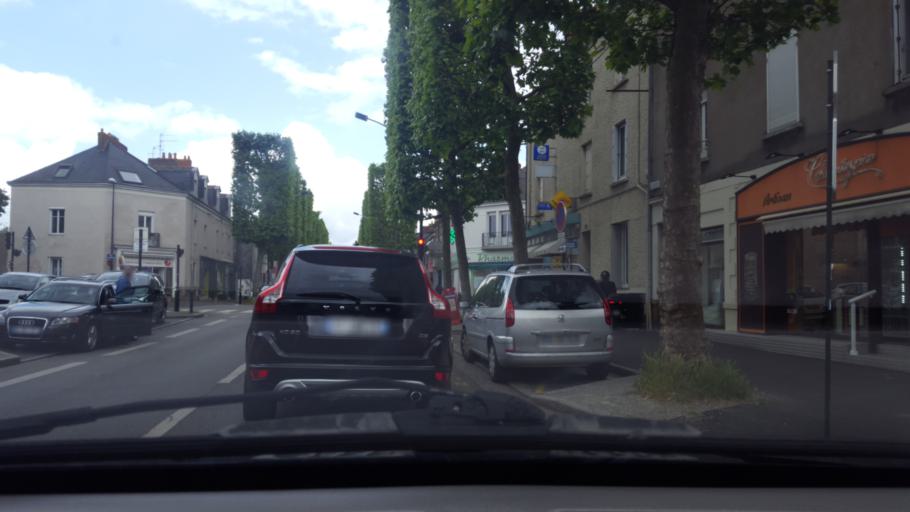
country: FR
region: Pays de la Loire
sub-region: Departement de la Loire-Atlantique
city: Nantes
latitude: 47.2064
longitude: -1.5879
